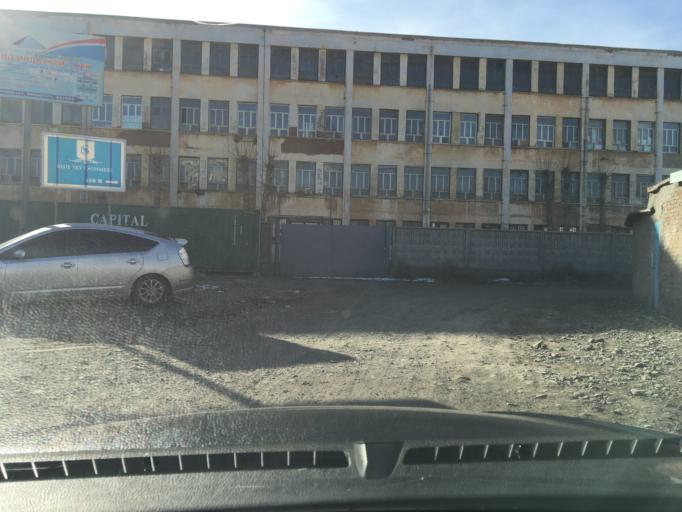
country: MN
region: Ulaanbaatar
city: Ulaanbaatar
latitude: 47.8939
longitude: 106.8932
